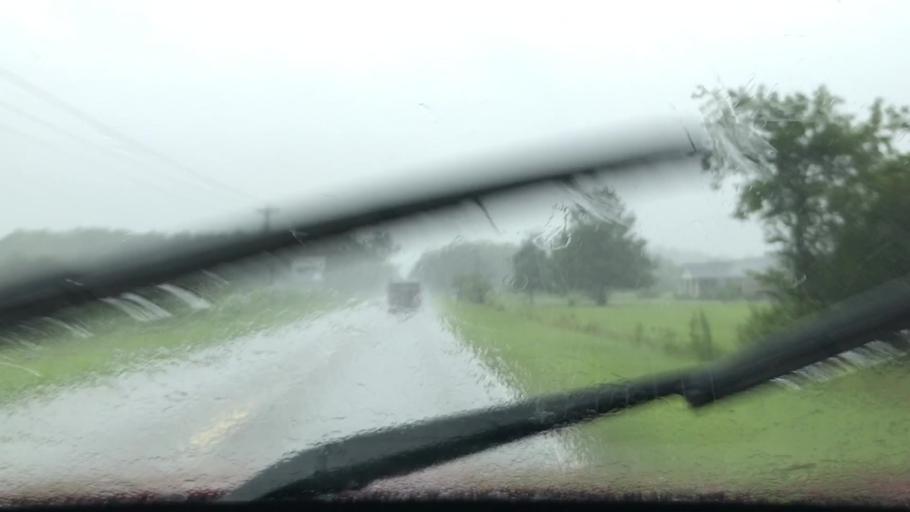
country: US
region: South Carolina
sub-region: Horry County
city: Red Hill
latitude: 33.8957
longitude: -78.9373
